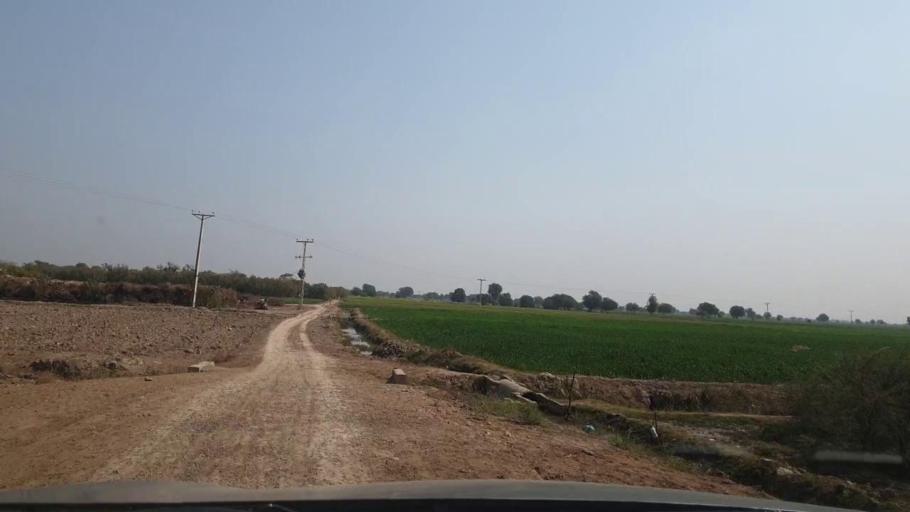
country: PK
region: Sindh
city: Tando Allahyar
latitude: 25.5440
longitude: 68.8160
